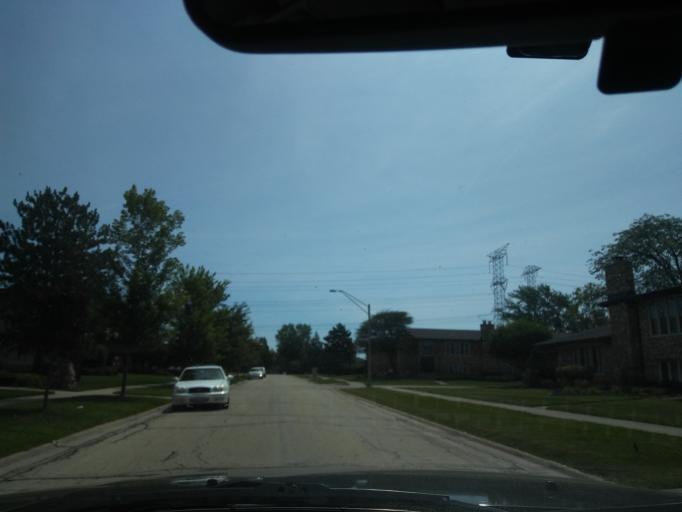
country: US
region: Illinois
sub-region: Cook County
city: Tinley Park
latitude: 41.6124
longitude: -87.8007
